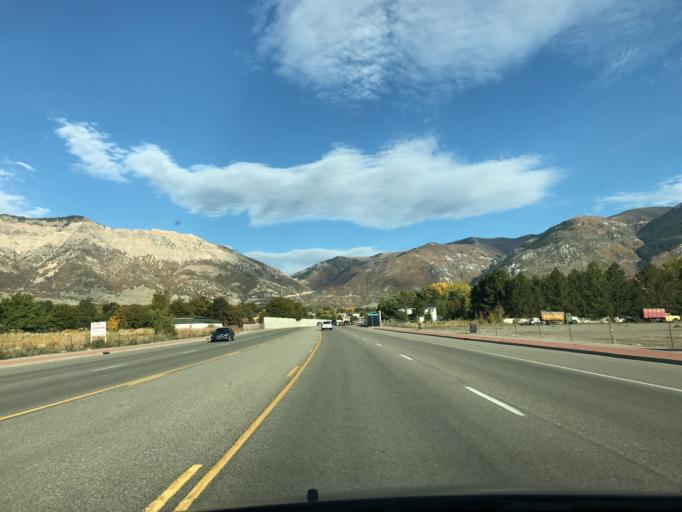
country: US
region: Utah
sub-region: Weber County
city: Pleasant View
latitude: 41.3056
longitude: -111.9800
